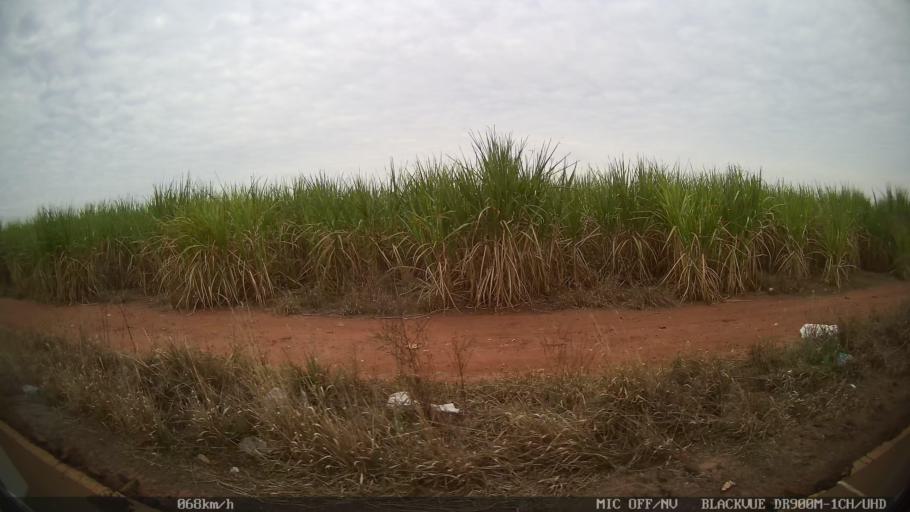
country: BR
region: Sao Paulo
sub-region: Cosmopolis
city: Cosmopolis
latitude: -22.6961
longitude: -47.1956
